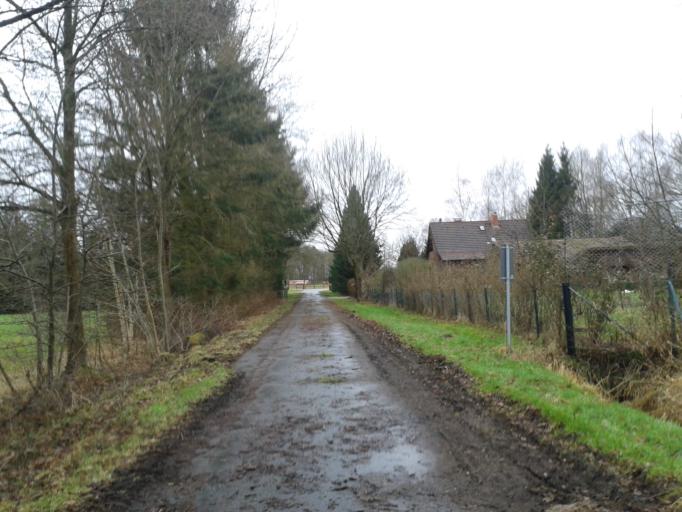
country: DE
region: Lower Saxony
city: Bergen an der Dumme
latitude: 52.9100
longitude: 10.9660
